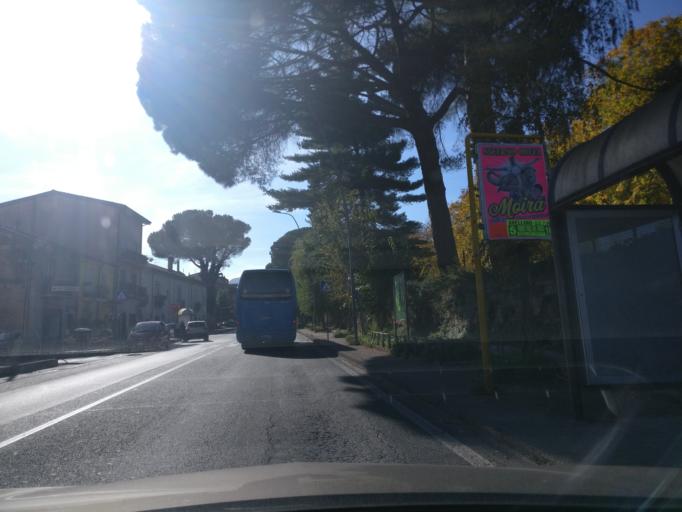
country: IT
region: Campania
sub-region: Provincia di Avellino
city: Torelli-Torrette
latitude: 40.9104
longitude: 14.7694
